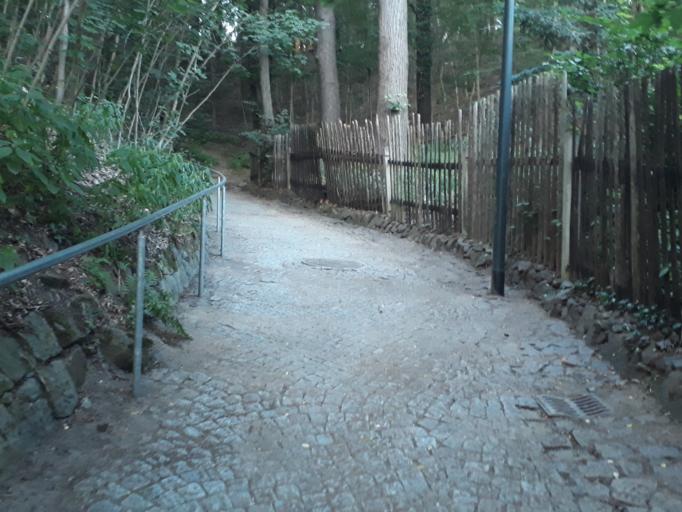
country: DE
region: Saxony
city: Heidenau
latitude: 51.0387
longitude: 13.8357
